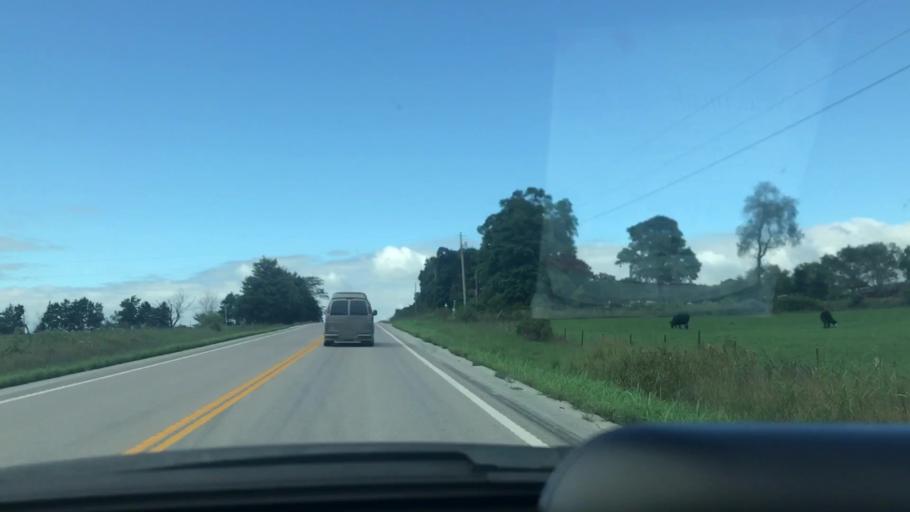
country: US
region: Missouri
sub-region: Hickory County
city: Hermitage
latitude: 37.9618
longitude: -93.2069
